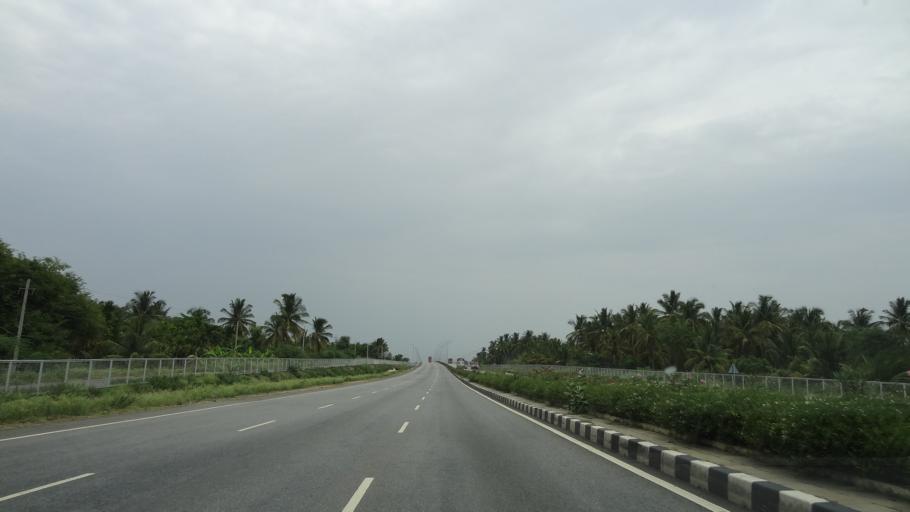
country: IN
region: Karnataka
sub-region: Tumkur
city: Sira
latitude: 13.7794
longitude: 76.8307
